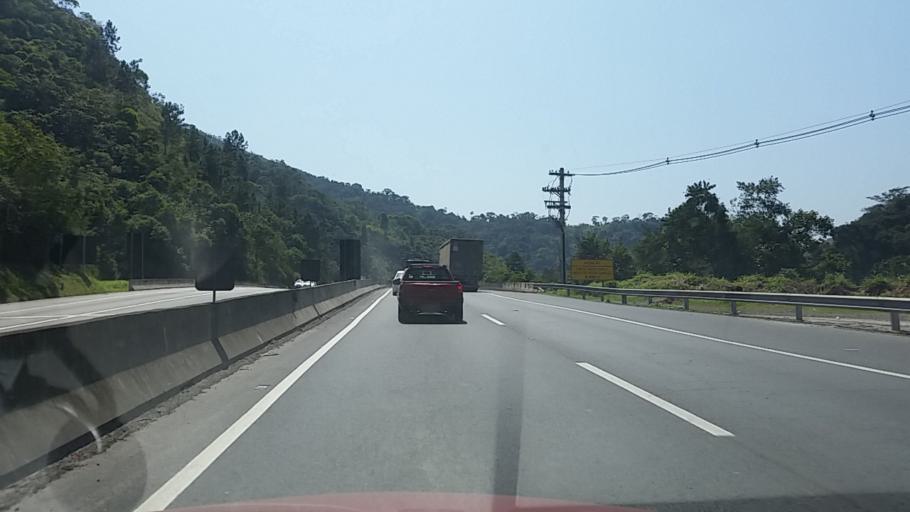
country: BR
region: Sao Paulo
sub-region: Miracatu
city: Miracatu
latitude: -24.1254
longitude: -47.2716
